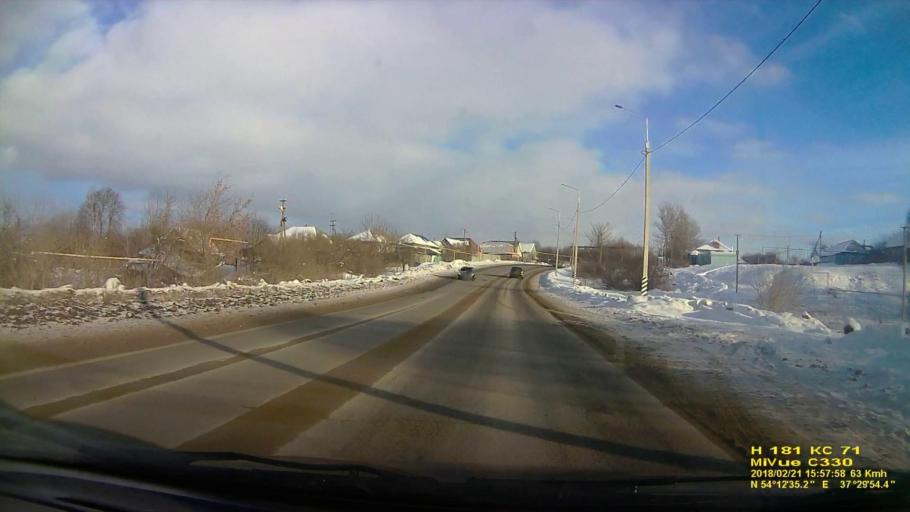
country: RU
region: Tula
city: Barsuki
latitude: 54.2097
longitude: 37.4989
